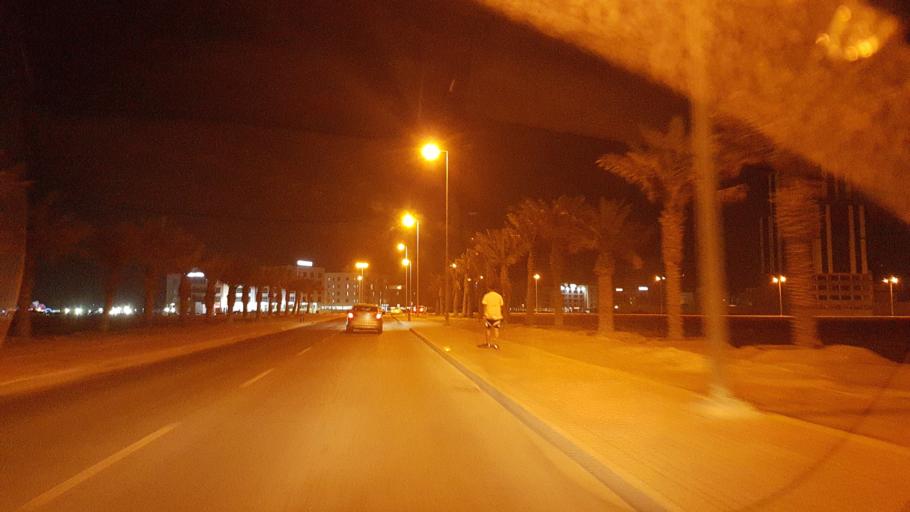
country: BH
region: Manama
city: Jidd Hafs
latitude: 26.2358
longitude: 50.5248
